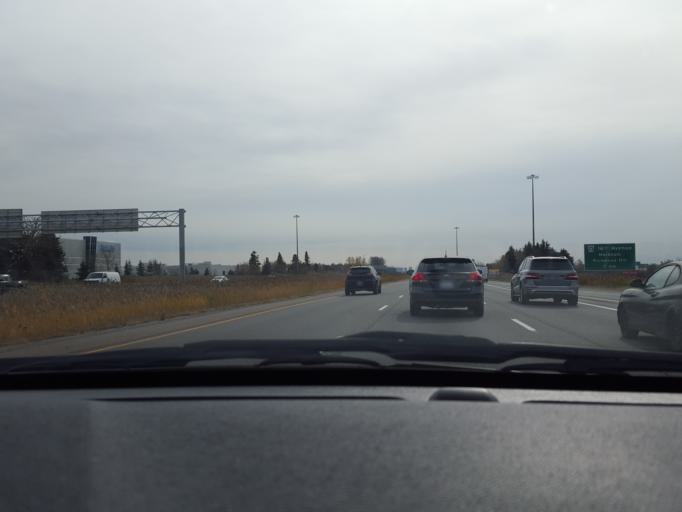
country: CA
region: Ontario
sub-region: York
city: Richmond Hill
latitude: 43.8789
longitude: -79.3790
